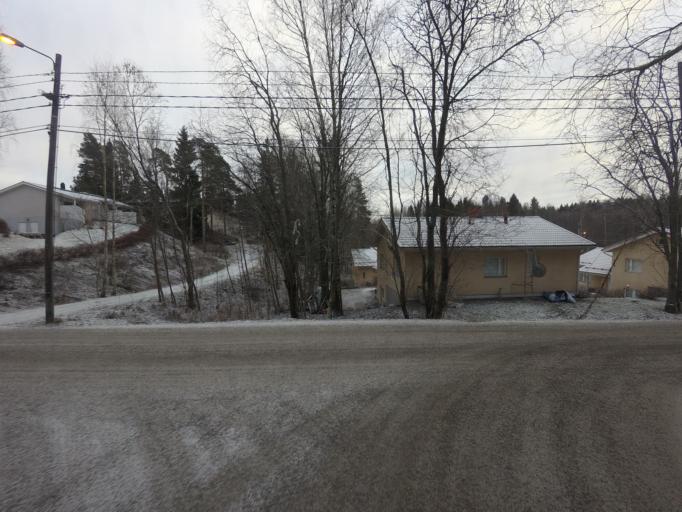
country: FI
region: Uusimaa
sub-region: Helsinki
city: Kauniainen
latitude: 60.2021
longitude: 24.6964
